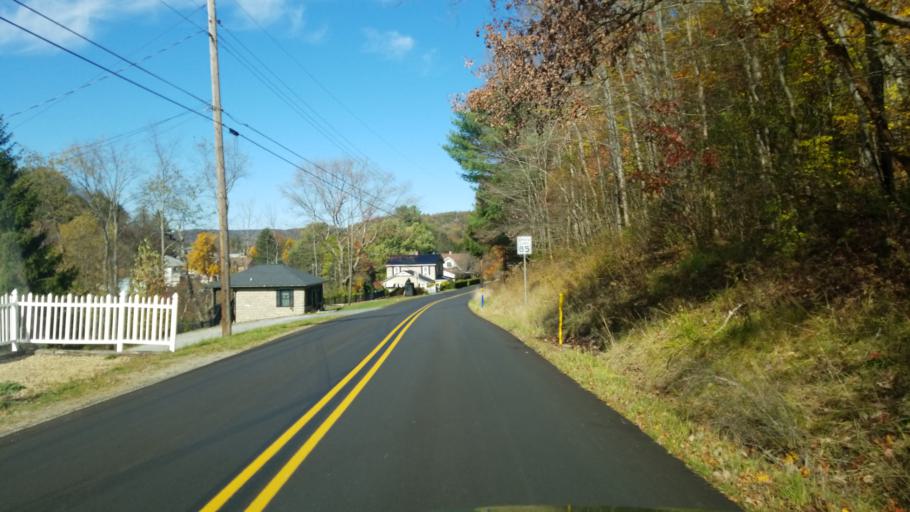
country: US
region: Pennsylvania
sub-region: Jefferson County
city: Brockway
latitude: 41.2438
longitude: -78.7963
